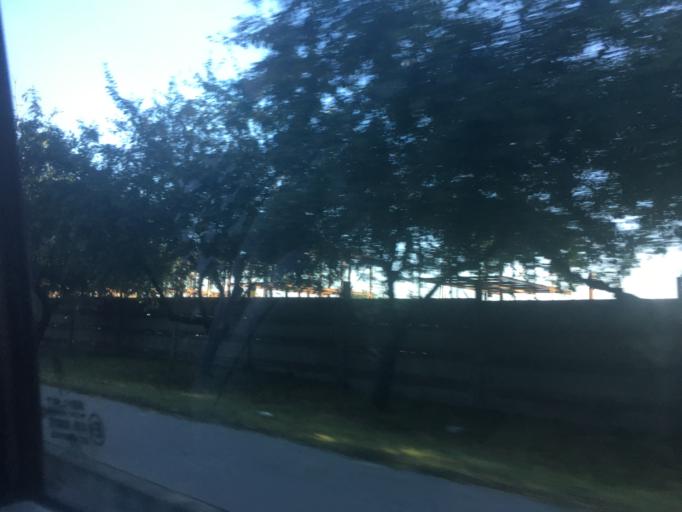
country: HU
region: Budapest
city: Budapest X. keruelet
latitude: 47.4890
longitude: 19.1684
